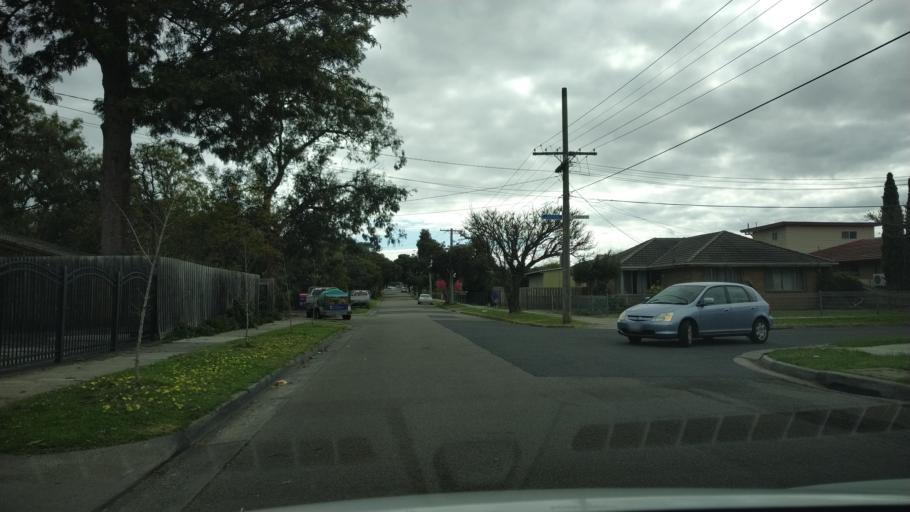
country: AU
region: Victoria
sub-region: Greater Dandenong
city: Springvale South
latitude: -37.9732
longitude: 145.1546
